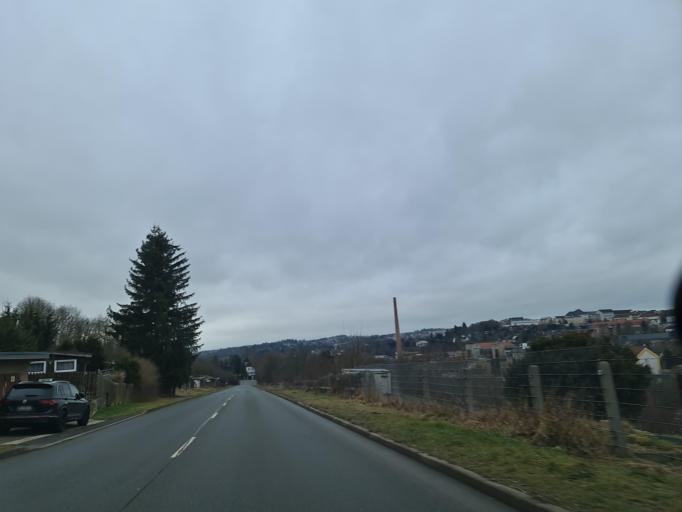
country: DE
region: Saxony
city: Plauen
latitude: 50.4853
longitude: 12.1342
